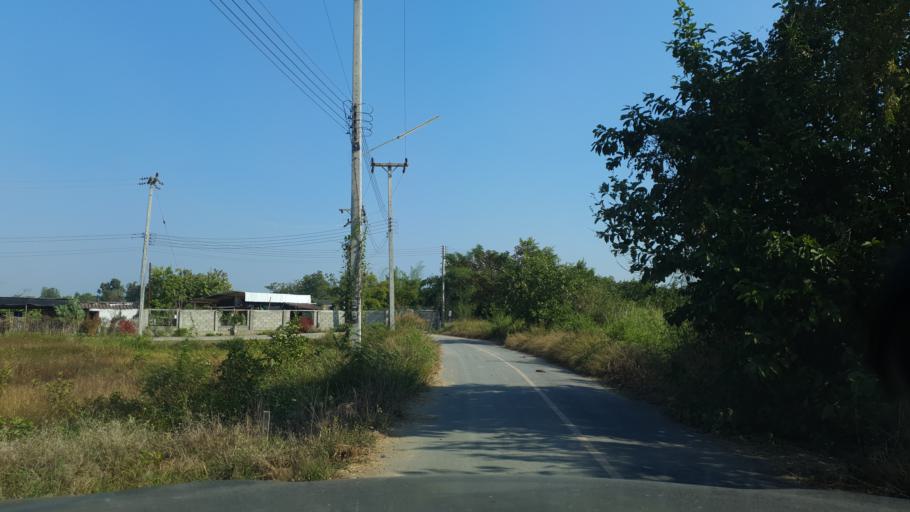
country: TH
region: Lamphun
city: Ban Thi
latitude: 18.6876
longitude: 99.0970
